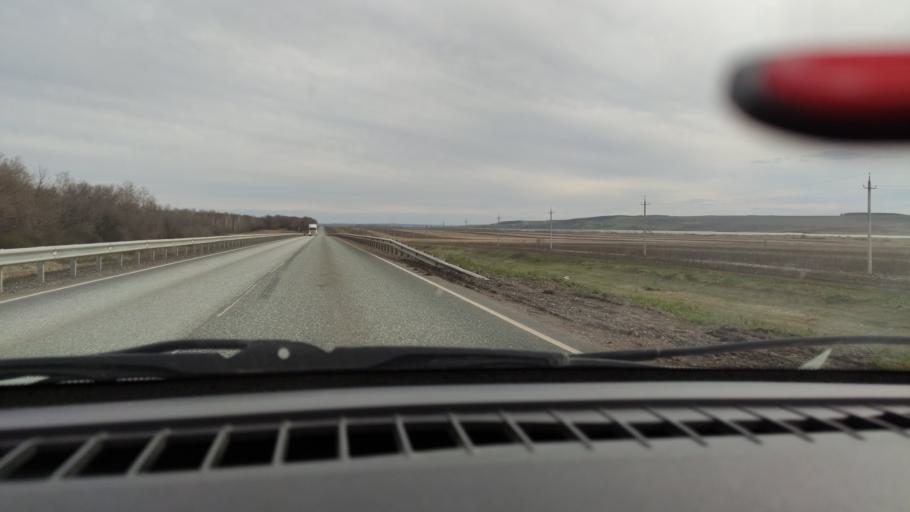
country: RU
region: Bashkortostan
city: Yermolayevo
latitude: 52.5445
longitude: 55.8359
